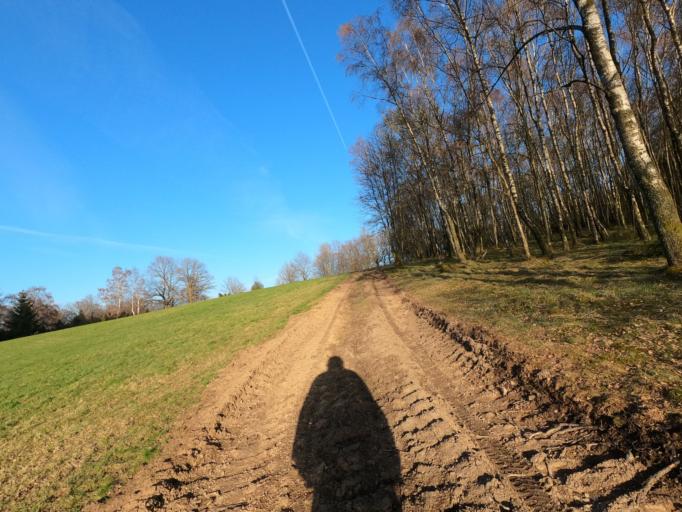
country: DE
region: North Rhine-Westphalia
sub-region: Regierungsbezirk Arnsberg
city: Herscheid
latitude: 51.1654
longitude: 7.7401
